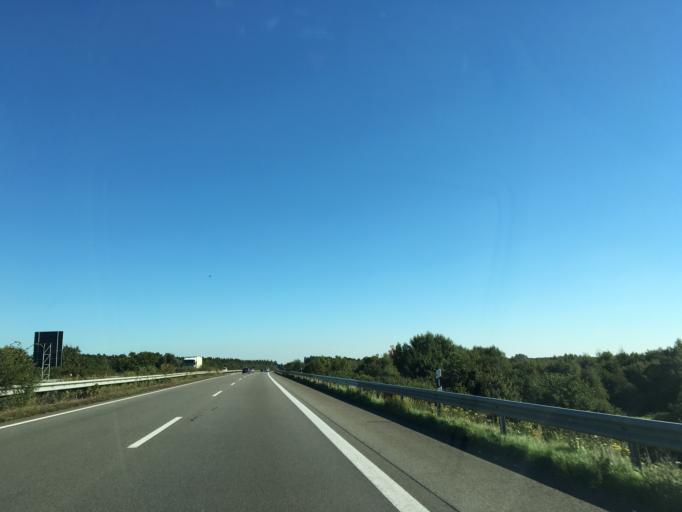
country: DE
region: Lower Saxony
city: Winsen
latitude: 53.3357
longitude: 10.2437
